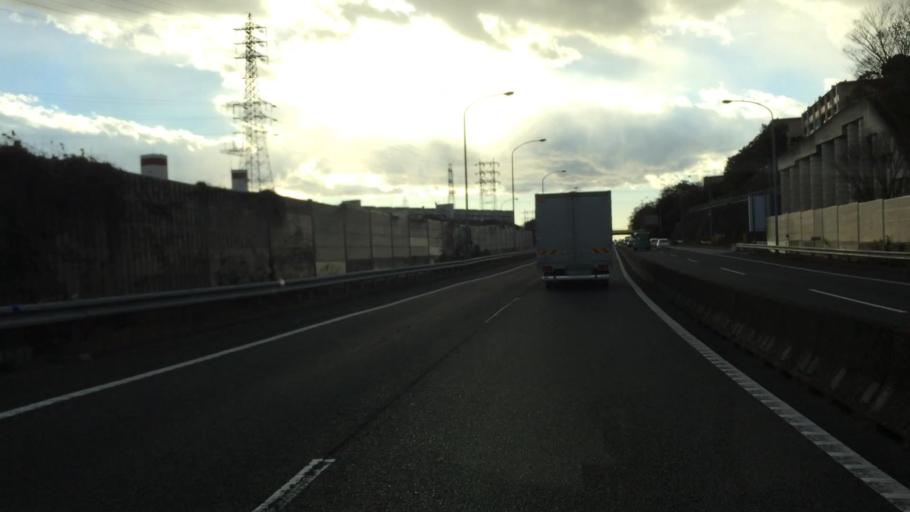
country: JP
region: Kanagawa
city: Yokohama
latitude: 35.4304
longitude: 139.5508
